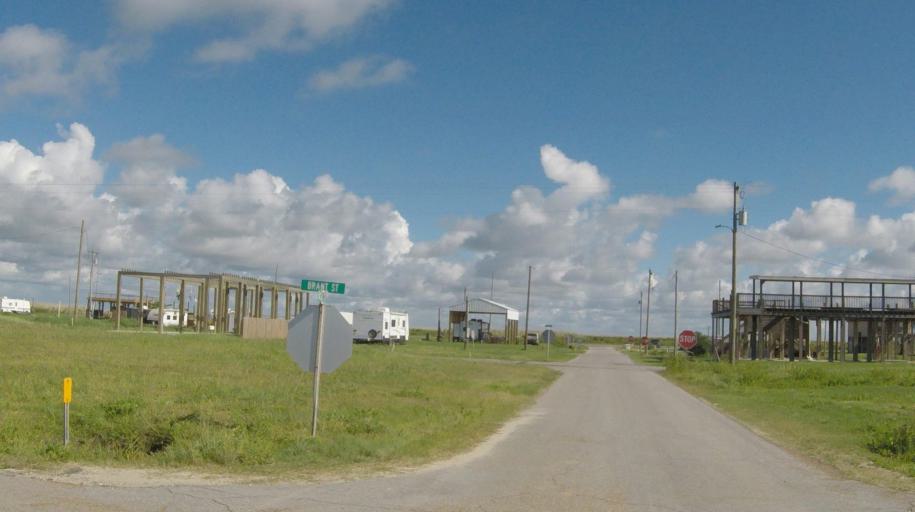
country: US
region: Louisiana
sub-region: Cameron Parish
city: Cameron
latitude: 29.7705
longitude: -93.4542
